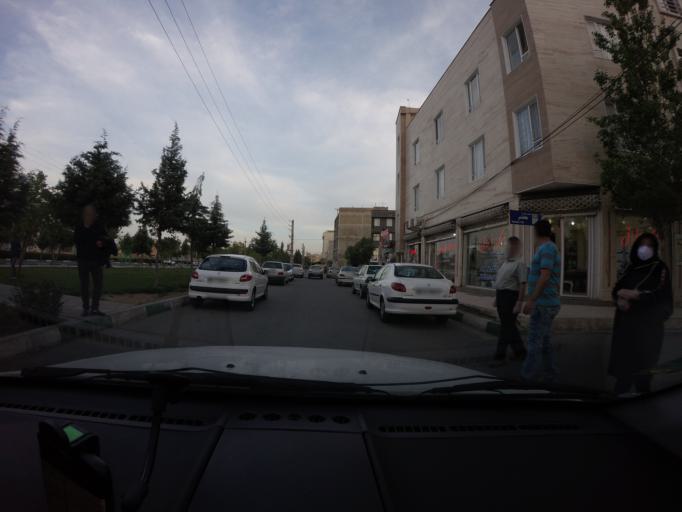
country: IR
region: Tehran
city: Eslamshahr
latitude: 35.5348
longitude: 51.2148
